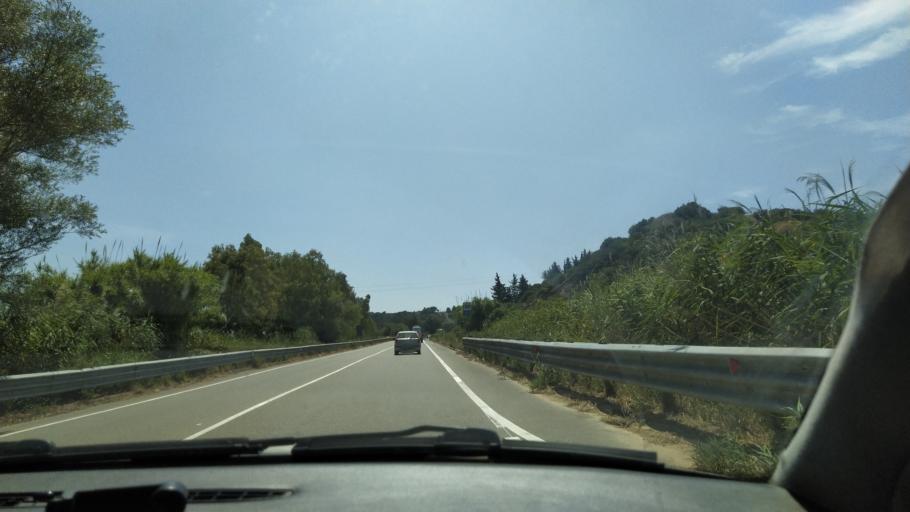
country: IT
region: Apulia
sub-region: Provincia di Taranto
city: Marina di Ginosa
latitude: 40.4332
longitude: 16.7910
